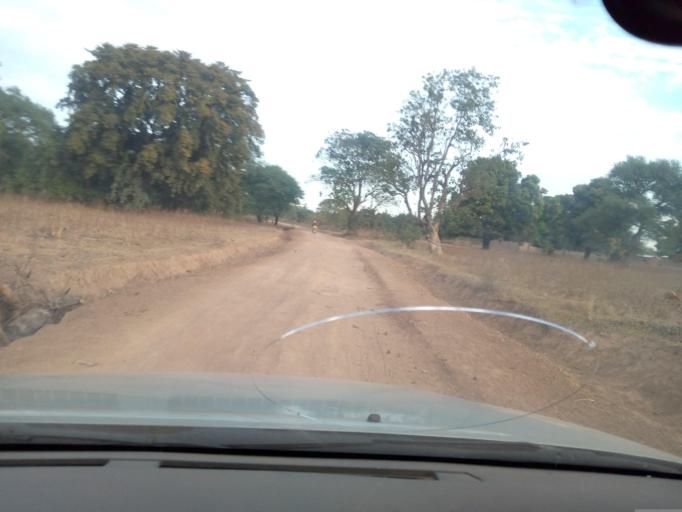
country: ML
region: Sikasso
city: Kadiolo
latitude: 10.5802
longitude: -5.8370
